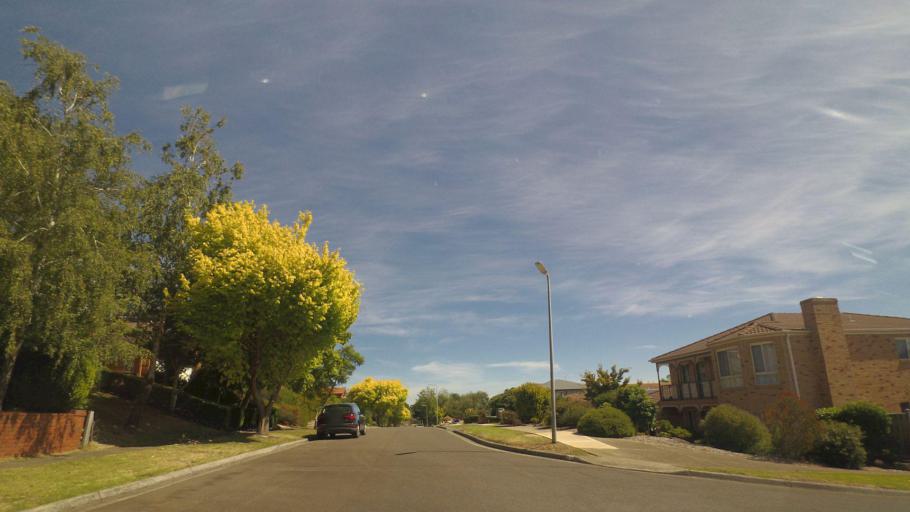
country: AU
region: Victoria
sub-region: Yarra Ranges
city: Chirnside Park
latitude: -37.7643
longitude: 145.3206
